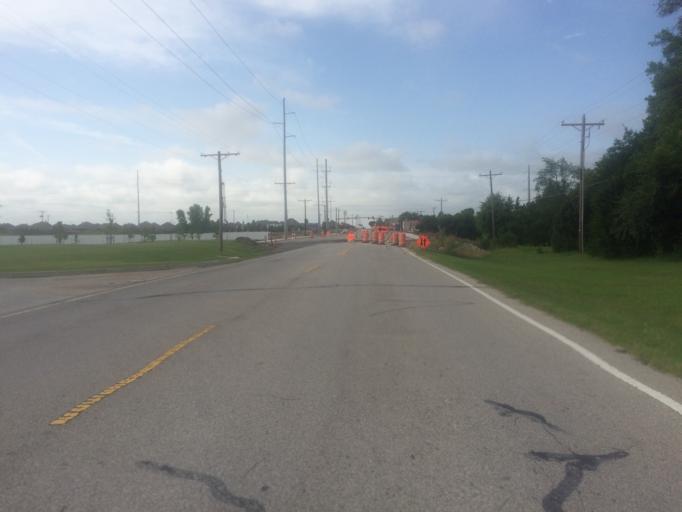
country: US
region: Oklahoma
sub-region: Cleveland County
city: Norman
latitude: 35.1778
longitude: -97.4237
